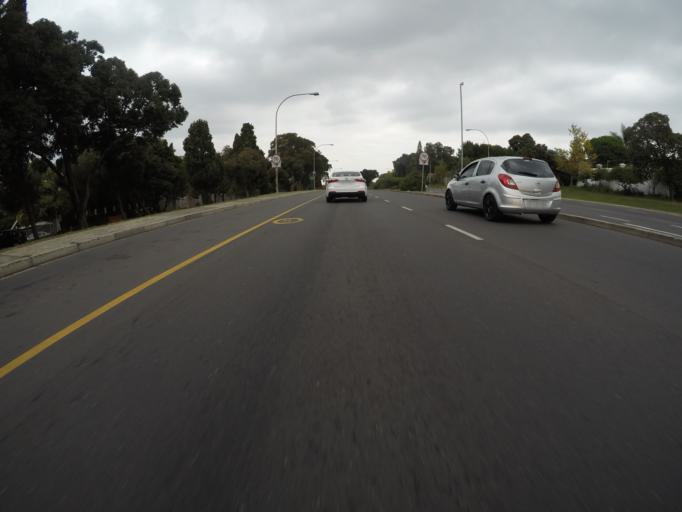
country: ZA
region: Western Cape
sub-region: City of Cape Town
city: Kraaifontein
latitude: -33.8537
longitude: 18.6438
